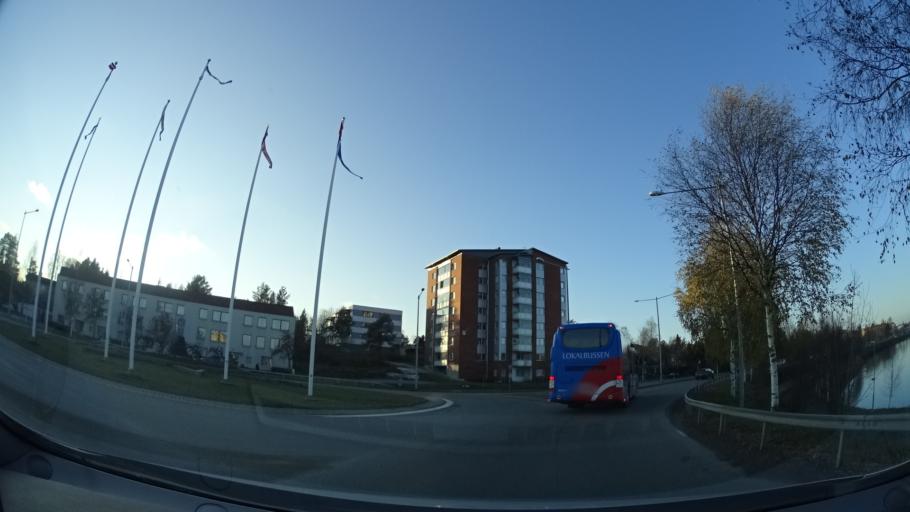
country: SE
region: Vaesterbotten
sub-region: Lycksele Kommun
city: Lycksele
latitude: 64.5901
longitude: 18.6845
